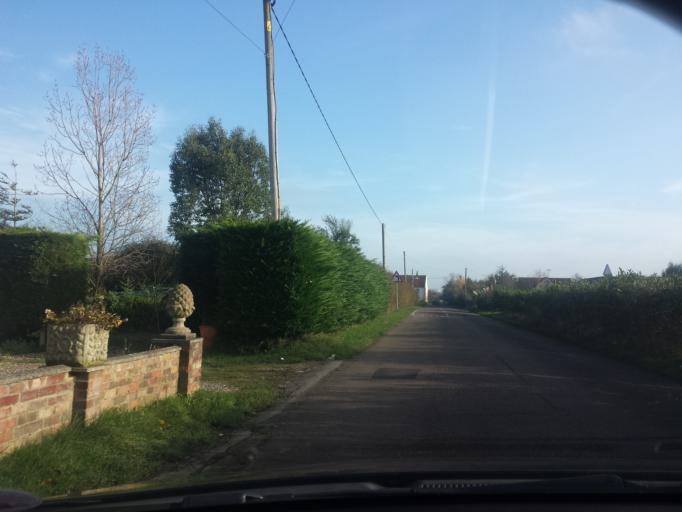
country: GB
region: England
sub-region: Essex
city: Saint Osyth
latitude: 51.8223
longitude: 1.1083
